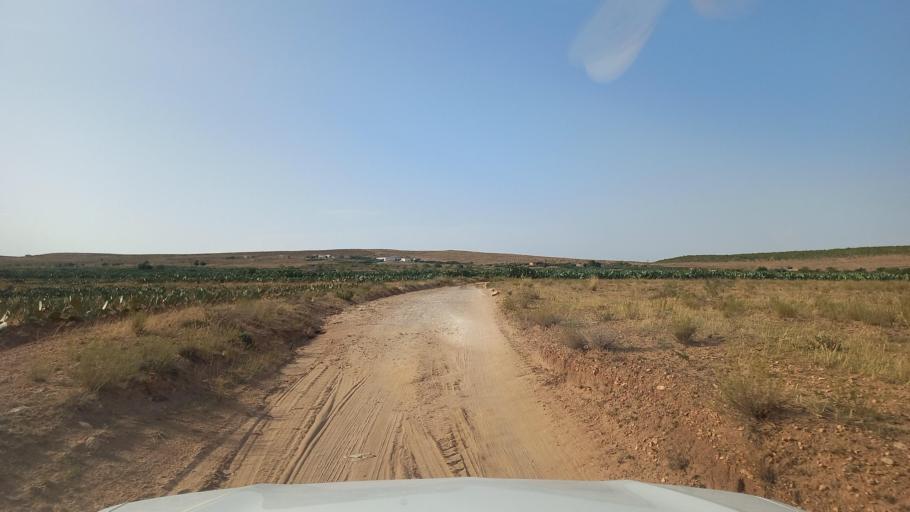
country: TN
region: Al Qasrayn
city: Kasserine
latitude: 35.3584
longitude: 8.8526
